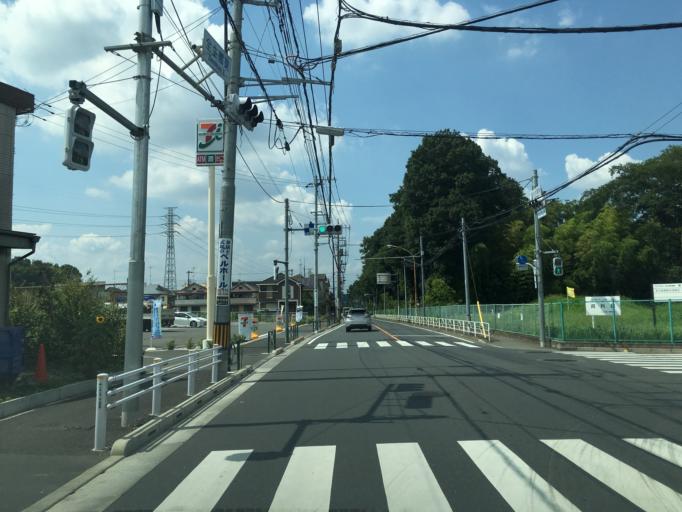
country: JP
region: Tokyo
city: Higashimurayama-shi
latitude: 35.7624
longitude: 139.4969
